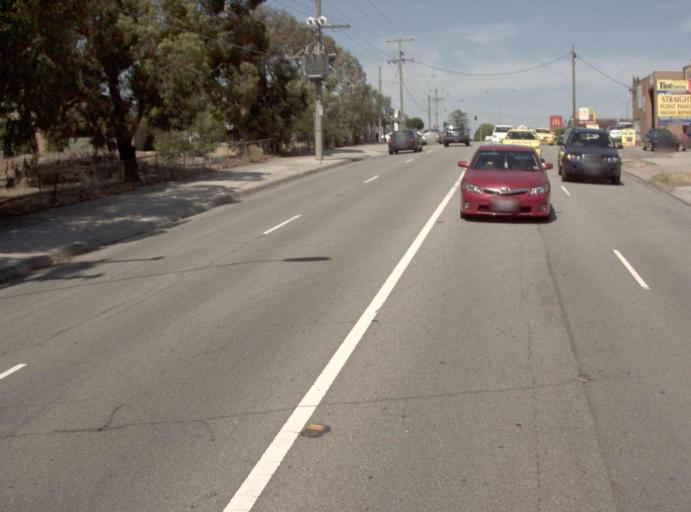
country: AU
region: Victoria
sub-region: Greater Dandenong
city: Noble Park North
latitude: -37.9603
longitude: 145.1904
